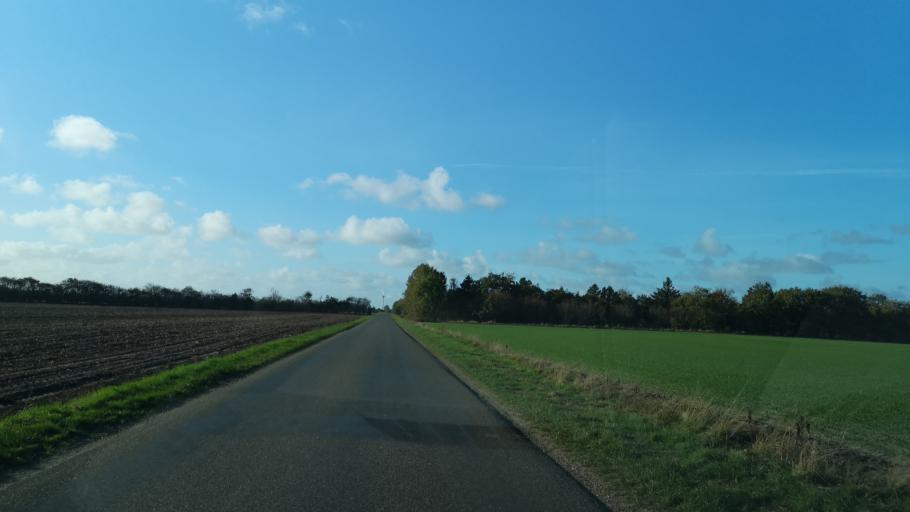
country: DK
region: Central Jutland
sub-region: Ringkobing-Skjern Kommune
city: Skjern
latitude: 55.8309
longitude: 8.3805
